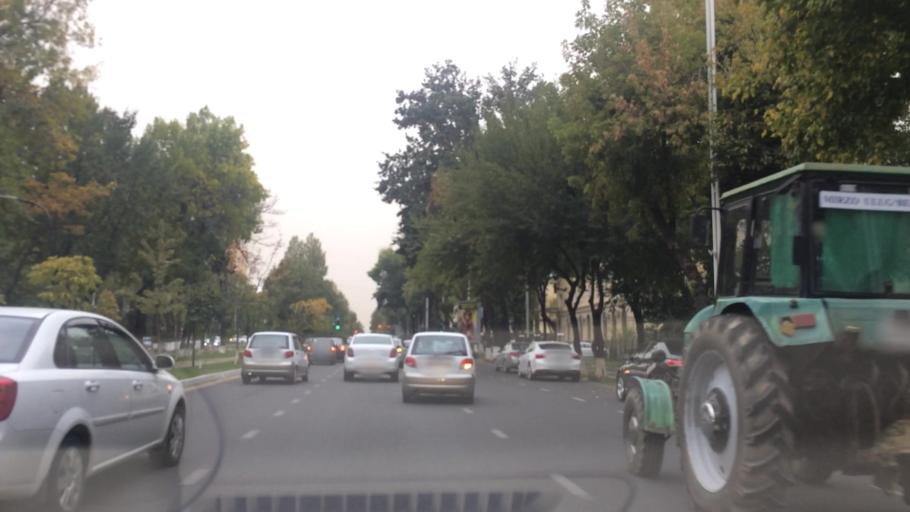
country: UZ
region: Toshkent Shahri
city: Tashkent
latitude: 41.3082
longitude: 69.2906
